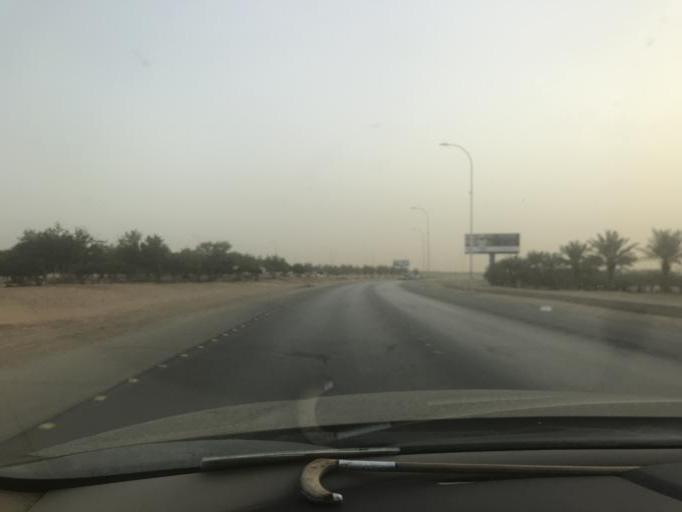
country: SA
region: Ar Riyad
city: Riyadh
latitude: 24.9040
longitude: 46.7120
